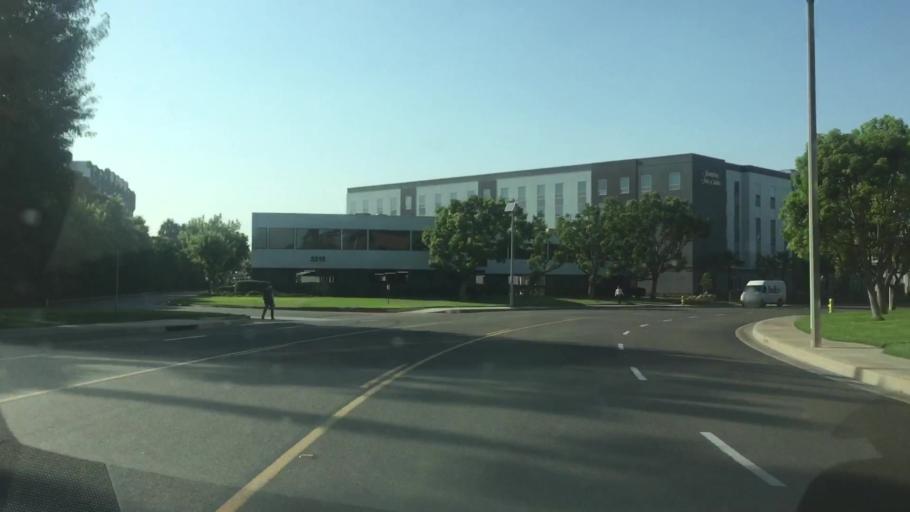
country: US
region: California
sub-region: Orange County
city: Irvine
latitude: 33.6736
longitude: -117.8580
